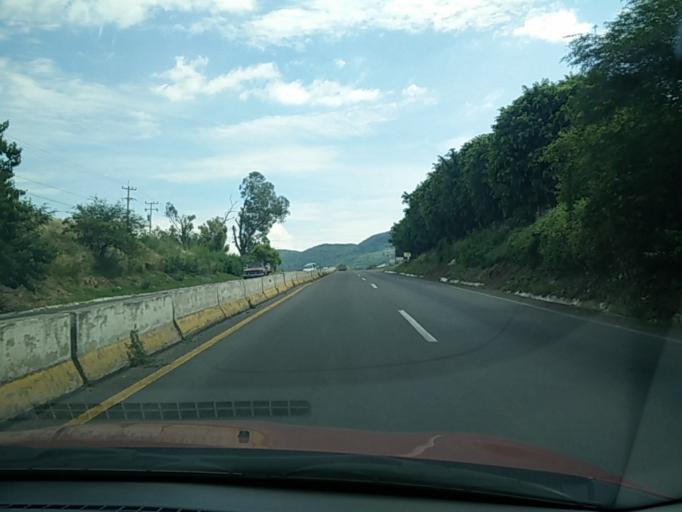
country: MX
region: Jalisco
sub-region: Ixtlahuacan de los Membrillos
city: Los Cedros
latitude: 20.3732
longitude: -103.2146
